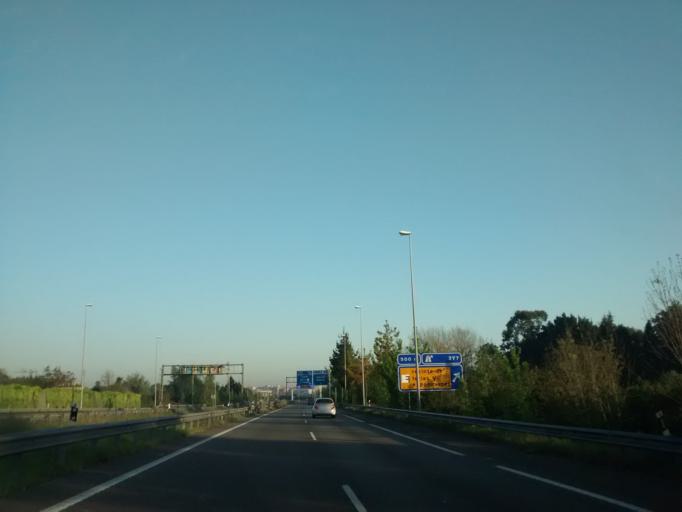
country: ES
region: Asturias
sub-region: Province of Asturias
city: Gijon
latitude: 43.5168
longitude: -5.6290
